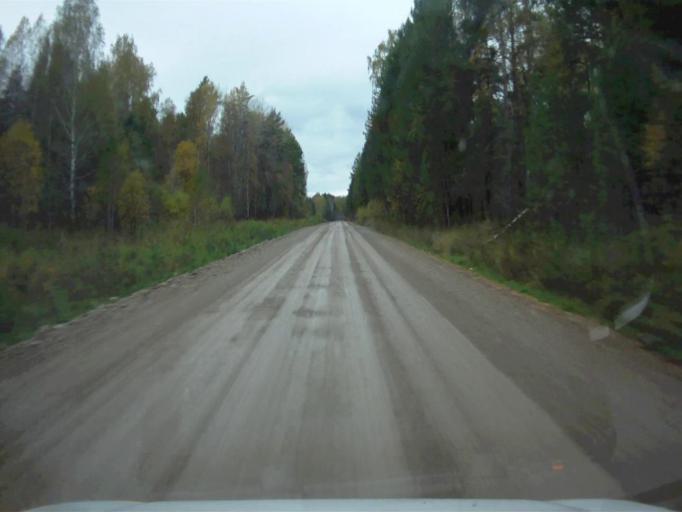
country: RU
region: Chelyabinsk
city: Nyazepetrovsk
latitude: 56.0945
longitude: 59.4042
